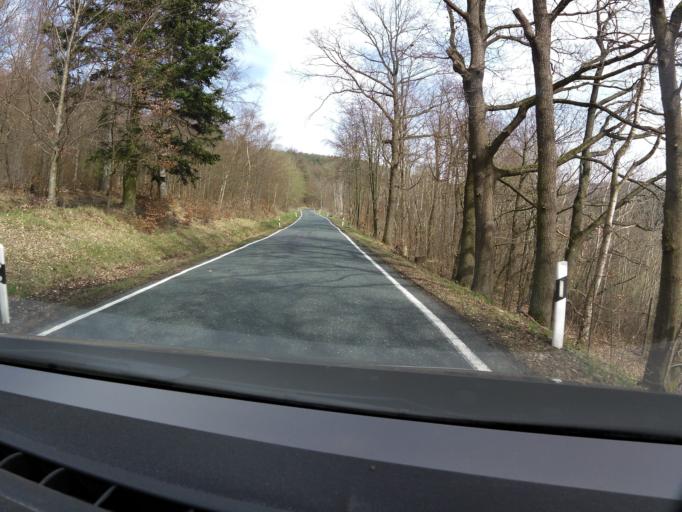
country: DE
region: Thuringia
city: Stadtlengsfeld
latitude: 50.7940
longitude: 10.1317
